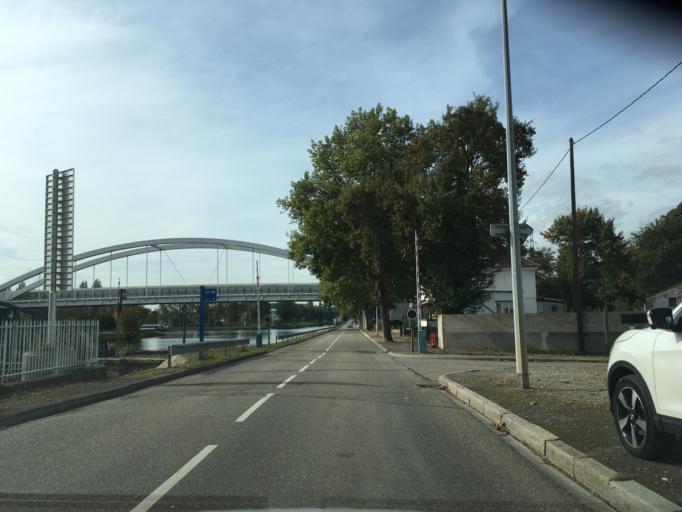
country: DE
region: Baden-Wuerttemberg
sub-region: Freiburg Region
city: Kehl
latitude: 48.5903
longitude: 7.7932
